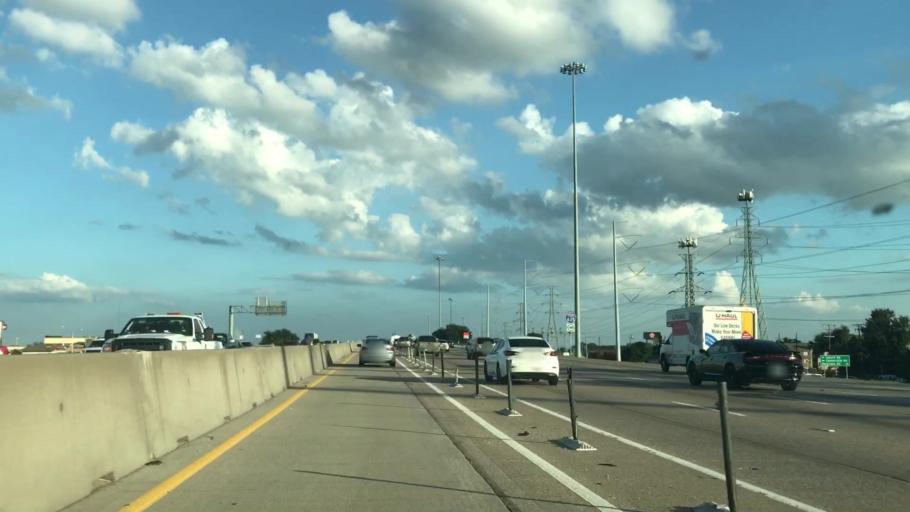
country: US
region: Texas
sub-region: Dallas County
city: Garland
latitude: 32.8572
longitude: -96.6509
